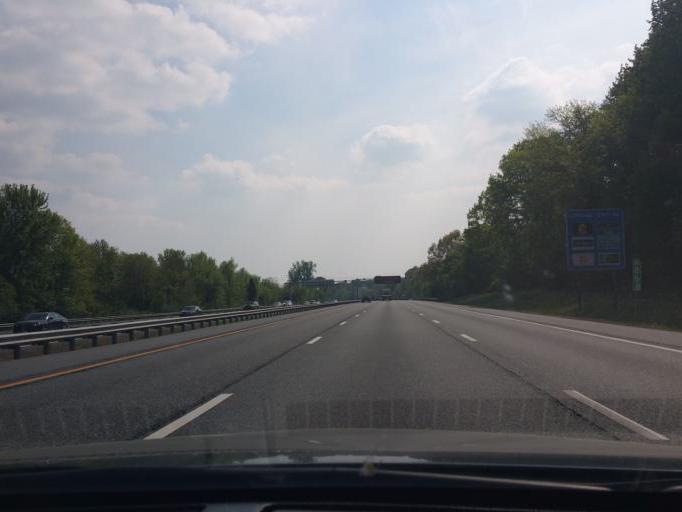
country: US
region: Maryland
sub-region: Harford County
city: Aberdeen
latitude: 39.5492
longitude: -76.1639
